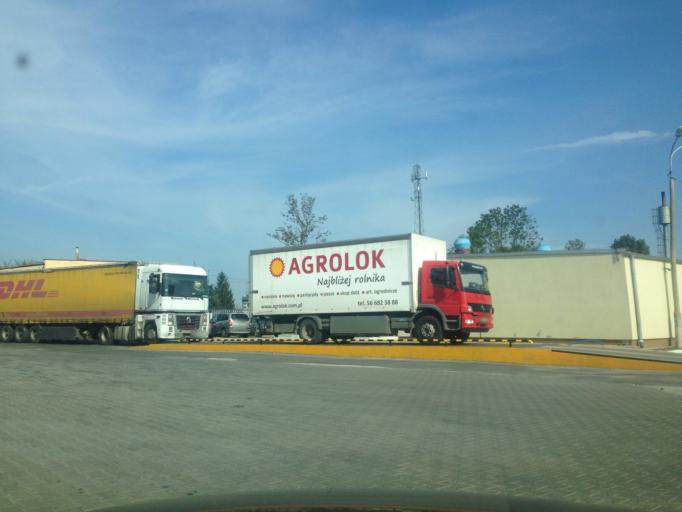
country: PL
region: Kujawsko-Pomorskie
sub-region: Powiat golubsko-dobrzynski
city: Golub-Dobrzyn
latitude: 53.1209
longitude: 19.0511
